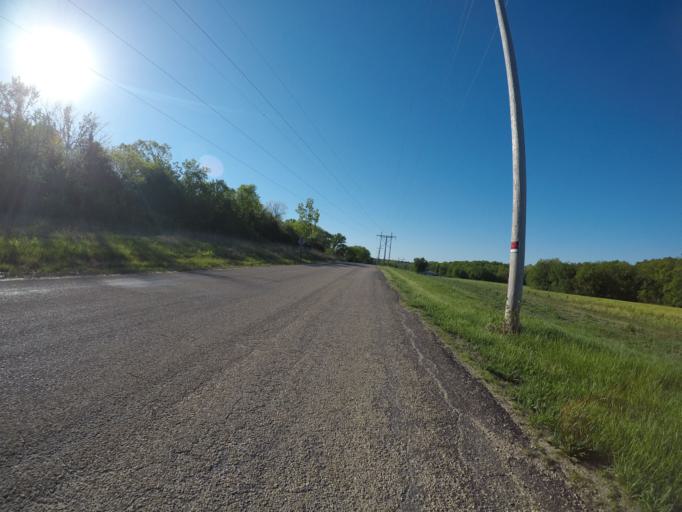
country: US
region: Kansas
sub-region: Shawnee County
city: Topeka
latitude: 39.0213
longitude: -95.5420
